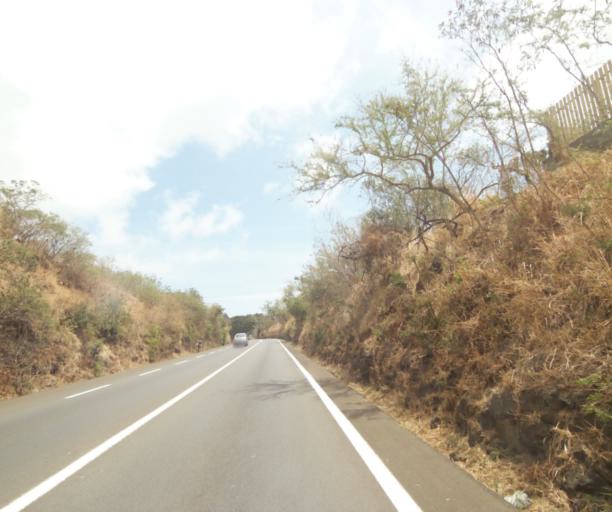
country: RE
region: Reunion
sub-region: Reunion
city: Saint-Paul
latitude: -21.0299
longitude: 55.2726
